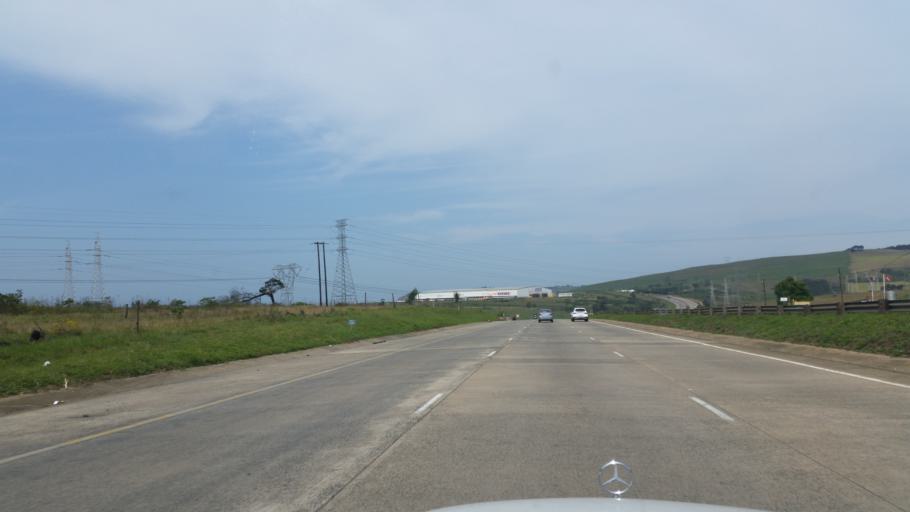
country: ZA
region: KwaZulu-Natal
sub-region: uMgungundlovu District Municipality
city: Camperdown
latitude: -29.7382
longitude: 30.6135
